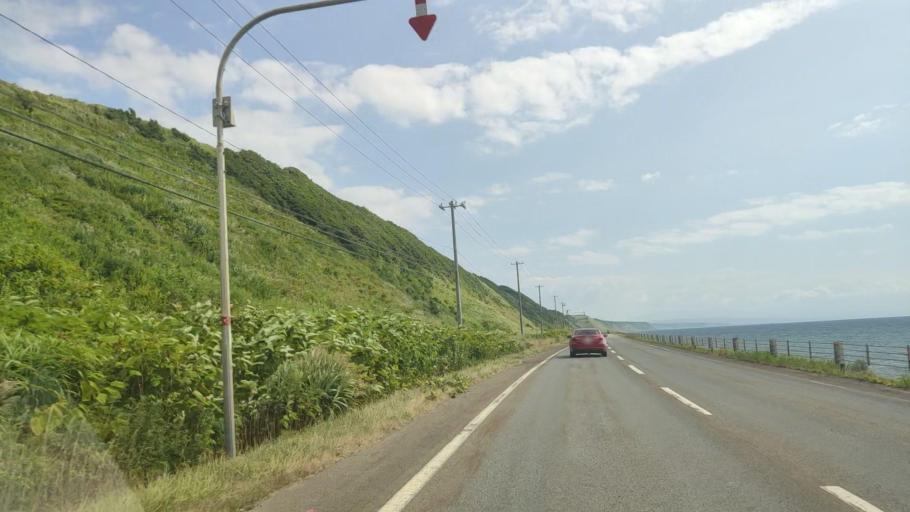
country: JP
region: Hokkaido
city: Rumoi
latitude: 44.0900
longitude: 141.6611
